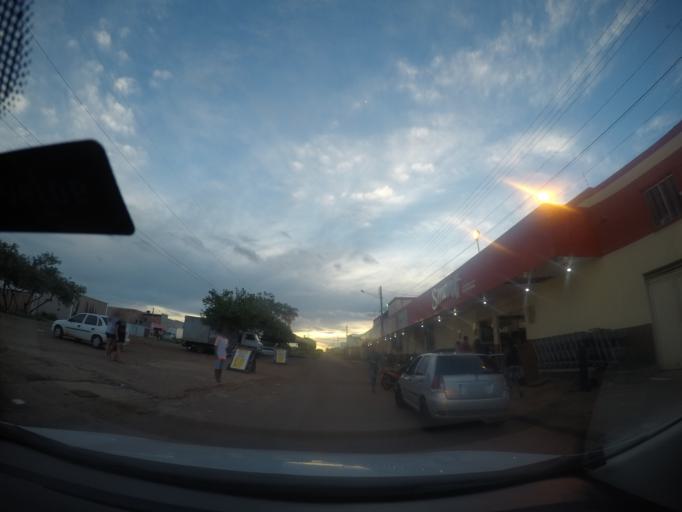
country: BR
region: Goias
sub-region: Goianira
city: Goianira
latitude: -16.5717
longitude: -49.3846
